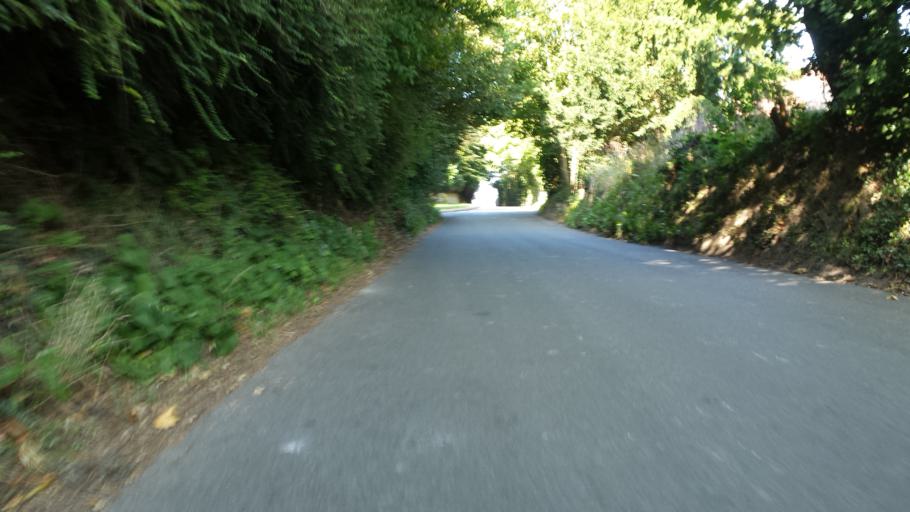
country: GB
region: England
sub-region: Kent
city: Eynsford
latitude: 51.3697
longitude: 0.2078
